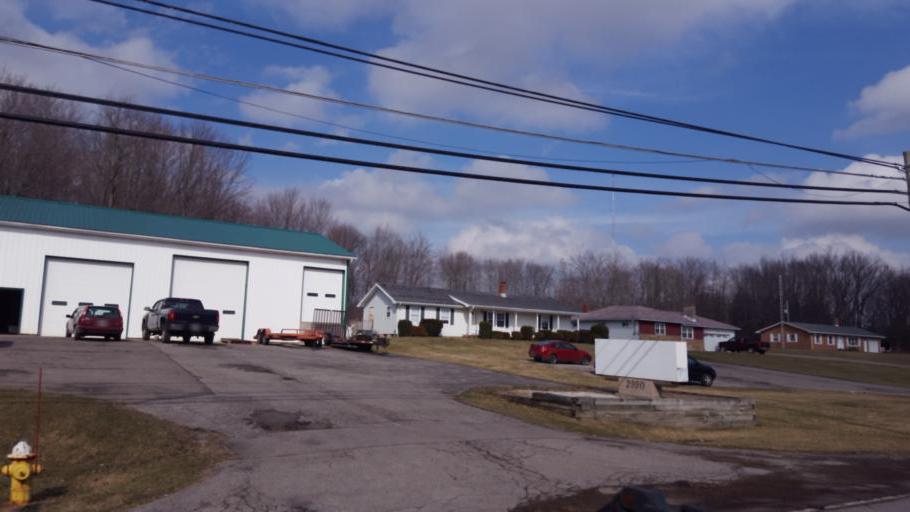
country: US
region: Ohio
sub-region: Richland County
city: Ontario
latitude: 40.7601
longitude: -82.6220
